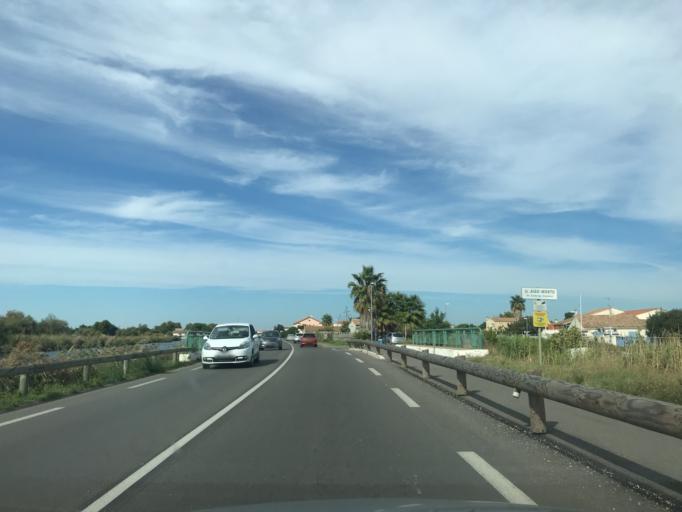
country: FR
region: Languedoc-Roussillon
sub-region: Departement du Gard
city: Aigues-Mortes
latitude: 43.5607
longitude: 4.1847
